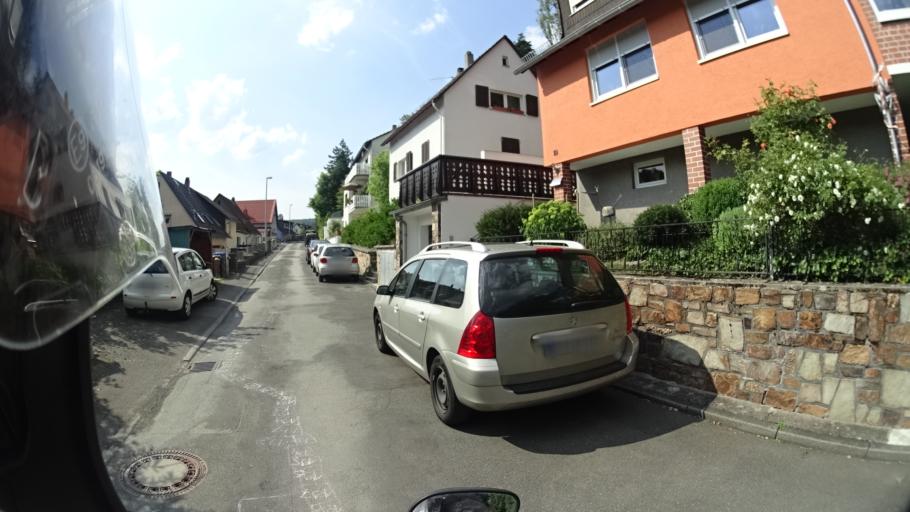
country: DE
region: Hesse
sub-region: Regierungsbezirk Darmstadt
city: Schlangenbad
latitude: 50.1069
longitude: 8.1014
